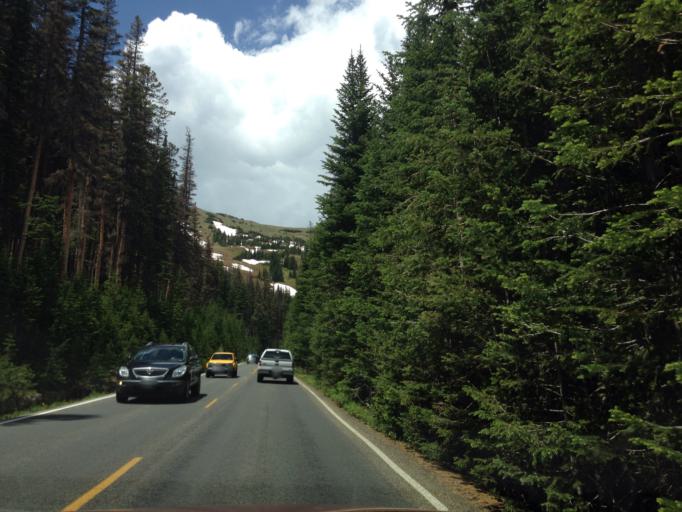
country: US
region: Colorado
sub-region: Larimer County
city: Estes Park
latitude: 40.3879
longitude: -105.6715
